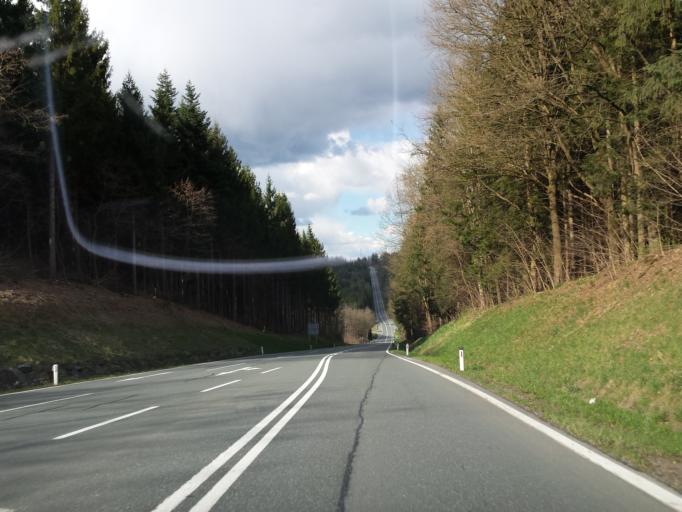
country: AT
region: Styria
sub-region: Politischer Bezirk Deutschlandsberg
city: Rassach
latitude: 46.8388
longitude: 15.2669
